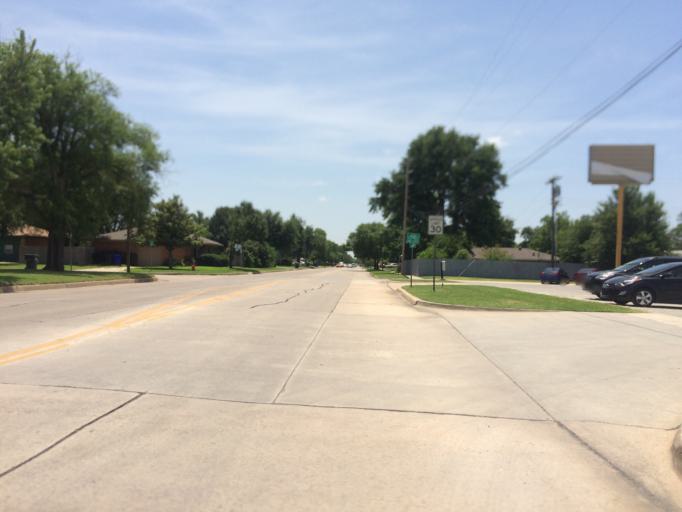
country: US
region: Oklahoma
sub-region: Cleveland County
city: Norman
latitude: 35.2324
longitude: -97.4591
